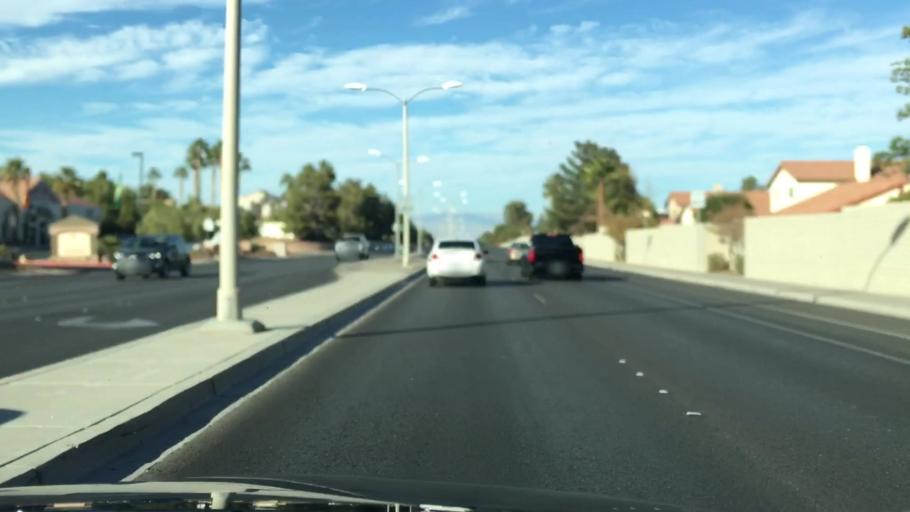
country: US
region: Nevada
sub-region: Clark County
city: Whitney
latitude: 36.0501
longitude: -115.1003
